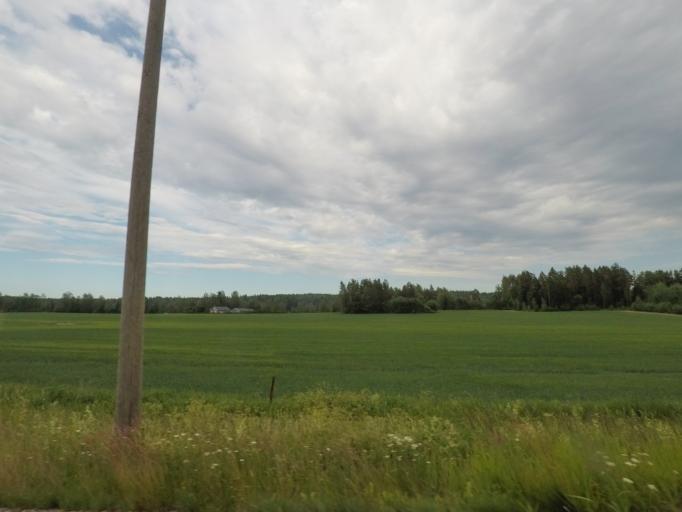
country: FI
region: Uusimaa
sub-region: Helsinki
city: Maentsaelae
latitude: 60.7526
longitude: 25.4324
